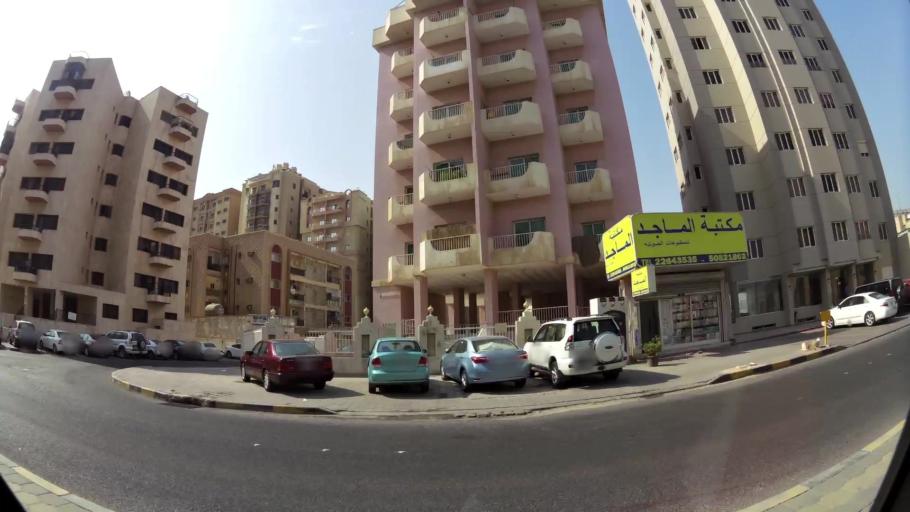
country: KW
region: Muhafazat Hawalli
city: Hawalli
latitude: 29.3387
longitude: 48.0277
